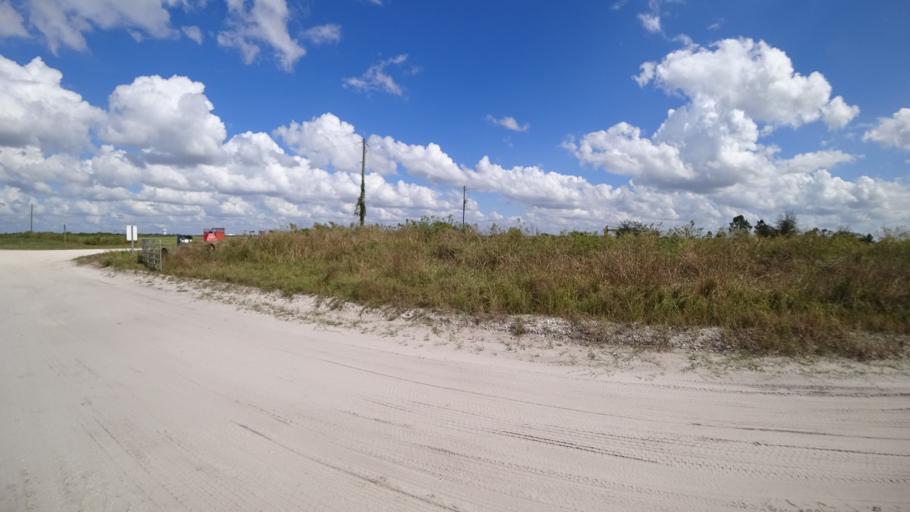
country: US
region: Florida
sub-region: Sarasota County
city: The Meadows
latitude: 27.4680
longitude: -82.3713
